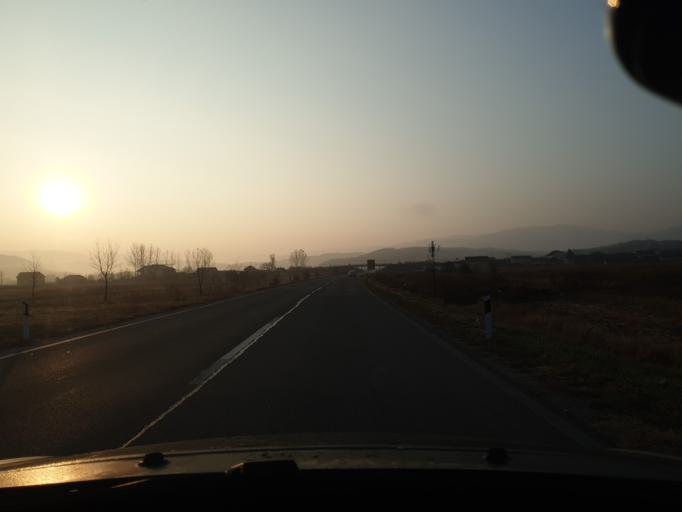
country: RS
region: Central Serbia
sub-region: Jablanicki Okrug
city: Leskovac
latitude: 42.9313
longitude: 22.0139
